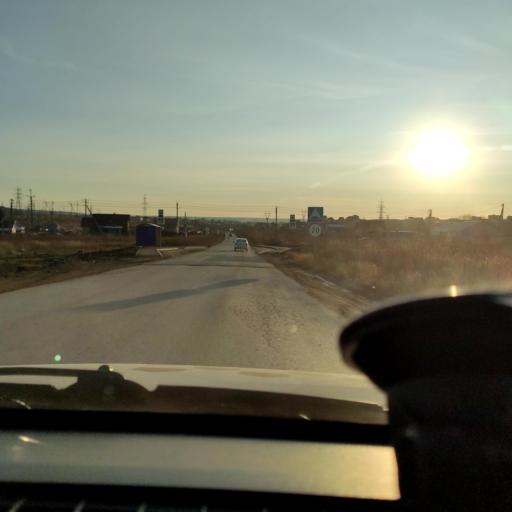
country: RU
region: Perm
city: Ferma
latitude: 57.9555
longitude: 56.3705
